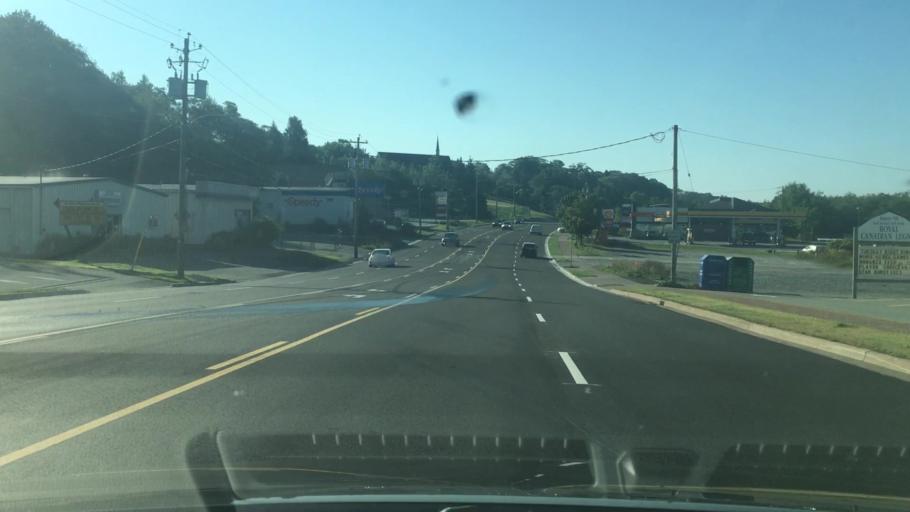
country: CA
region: Nova Scotia
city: Dartmouth
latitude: 44.7409
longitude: -63.6551
